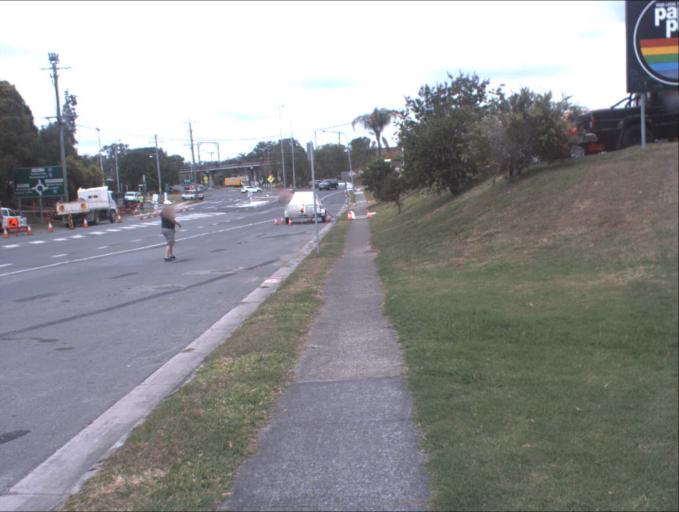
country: AU
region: Queensland
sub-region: Logan
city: Beenleigh
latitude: -27.7137
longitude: 153.1941
